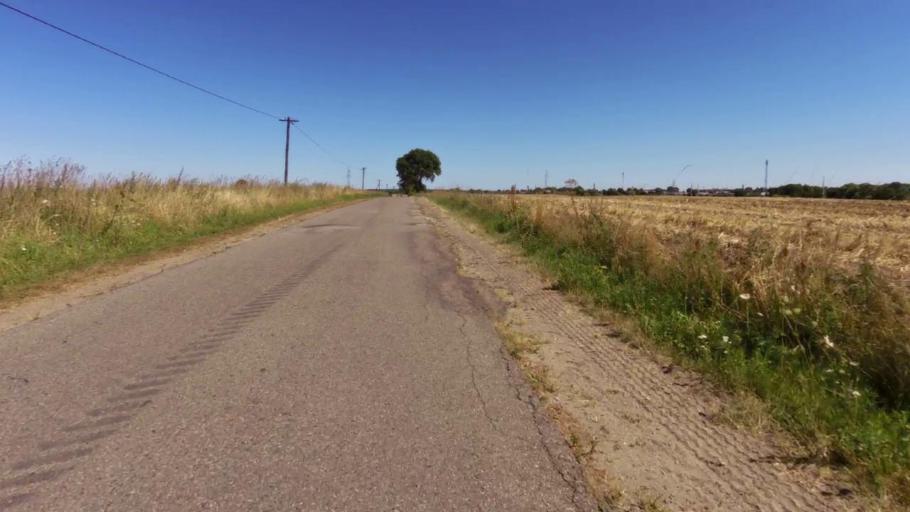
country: PL
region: West Pomeranian Voivodeship
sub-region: Powiat drawski
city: Czaplinek
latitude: 53.5469
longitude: 16.2132
